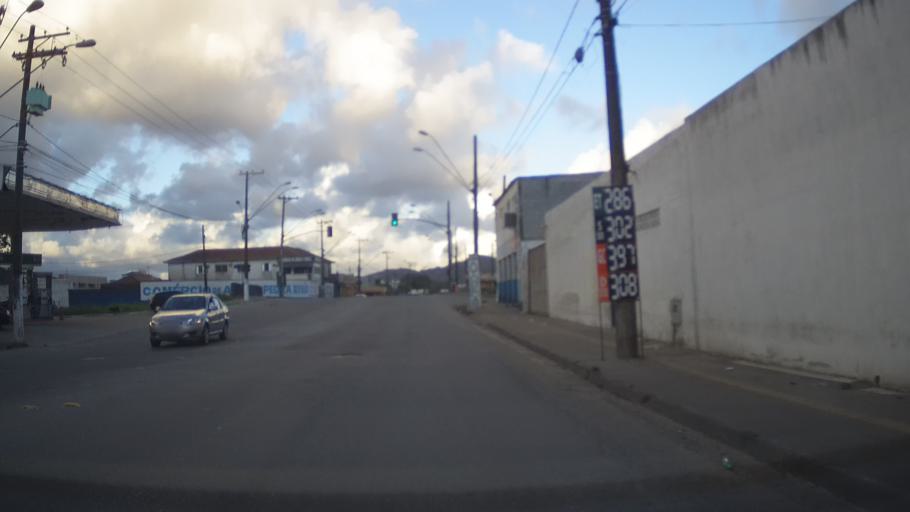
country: BR
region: Sao Paulo
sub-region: Sao Vicente
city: Sao Vicente
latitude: -23.9504
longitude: -46.4020
